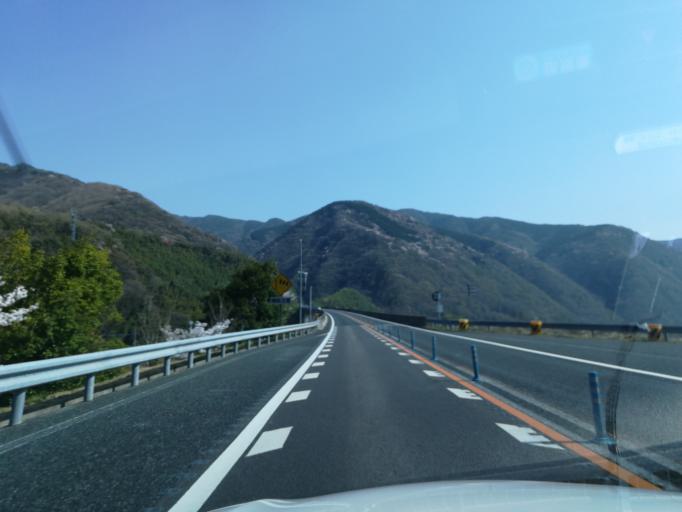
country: JP
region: Tokushima
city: Ikedacho
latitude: 34.0446
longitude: 133.9121
